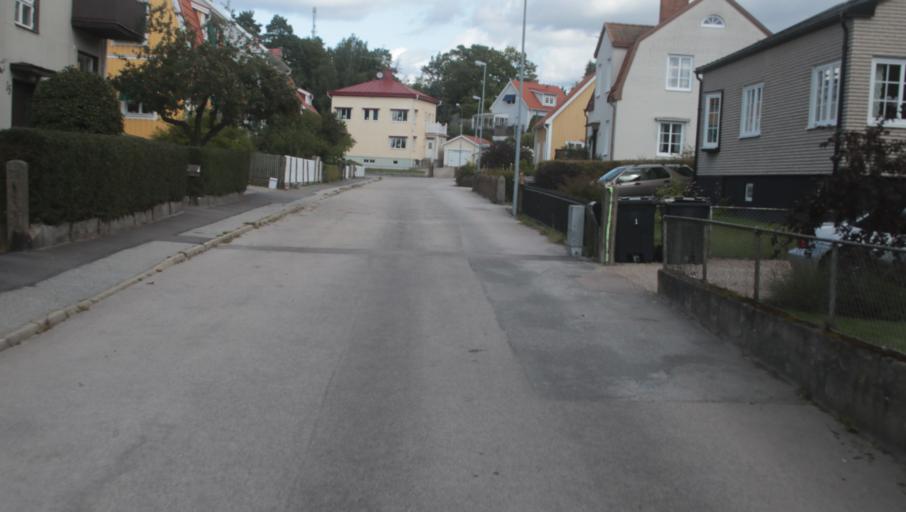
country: SE
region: Blekinge
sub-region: Karlshamns Kommun
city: Karlshamn
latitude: 56.1701
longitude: 14.8746
